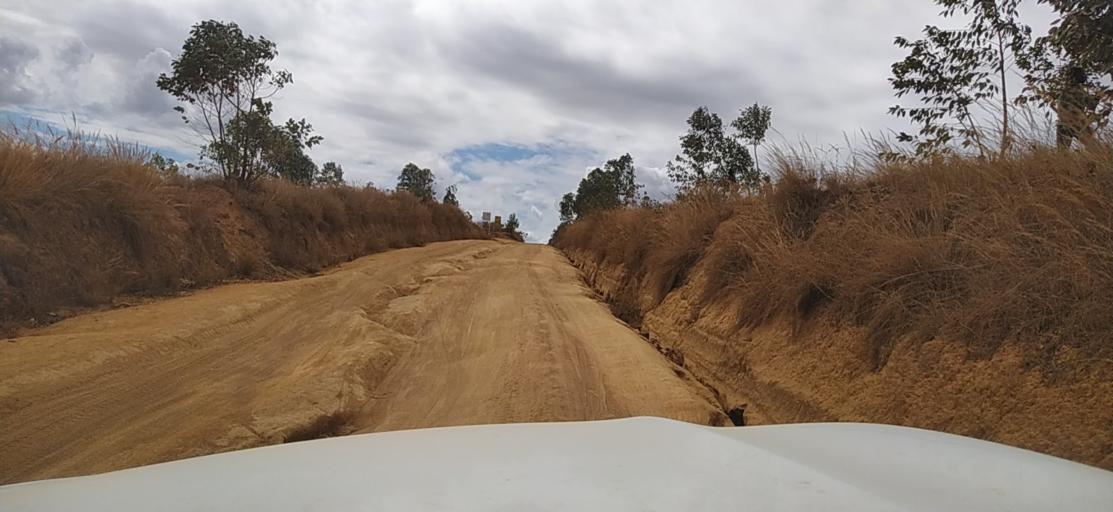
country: MG
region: Alaotra Mangoro
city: Ambatondrazaka
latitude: -17.9488
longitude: 48.2489
